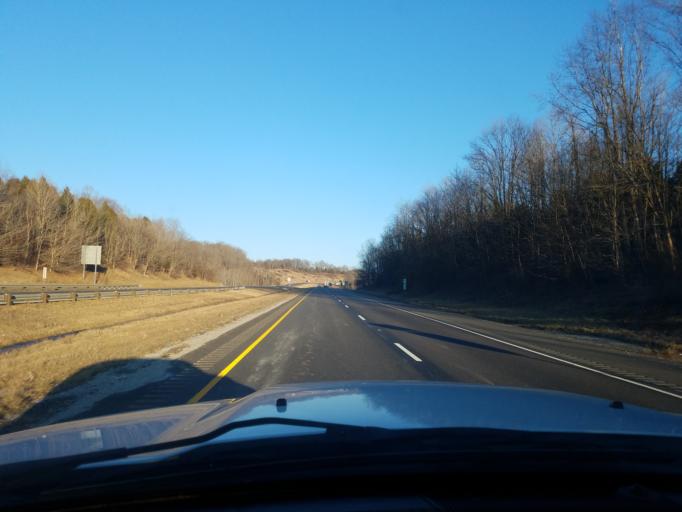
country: US
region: Indiana
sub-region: Crawford County
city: English
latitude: 38.2436
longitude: -86.4584
